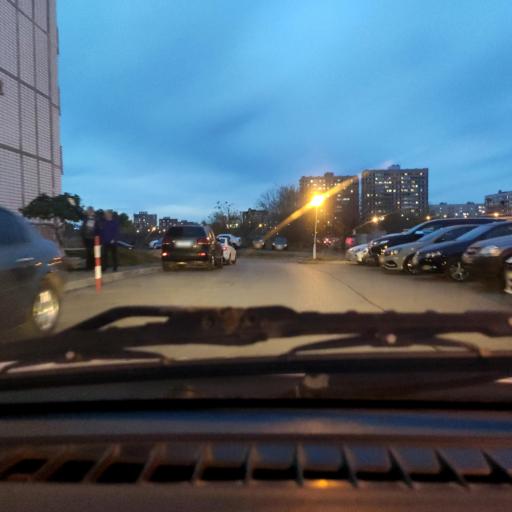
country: RU
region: Samara
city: Tol'yatti
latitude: 53.5254
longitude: 49.3344
